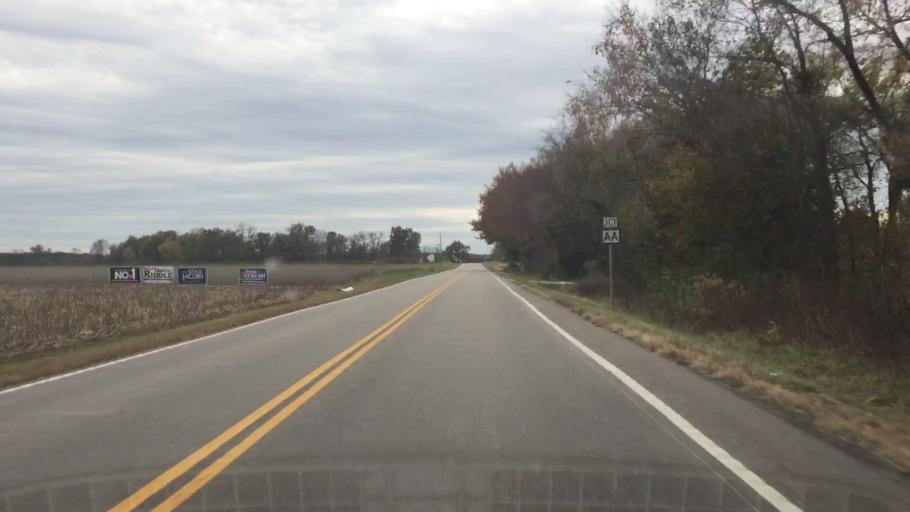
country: US
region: Missouri
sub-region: Callaway County
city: Holts Summit
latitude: 38.6064
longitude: -91.9891
